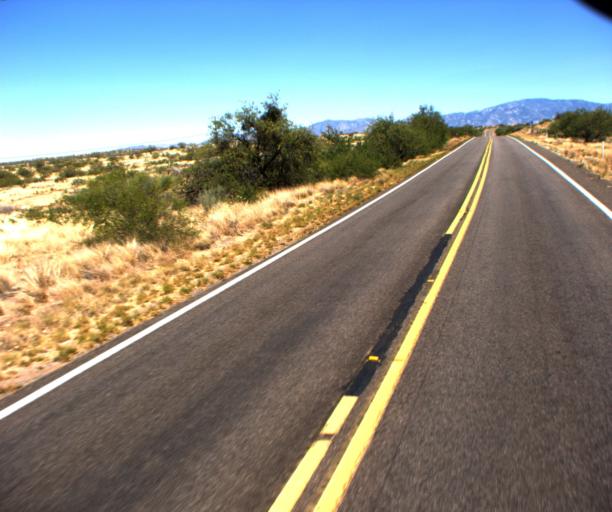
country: US
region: Arizona
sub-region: Pima County
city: Catalina
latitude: 32.6223
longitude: -110.9962
